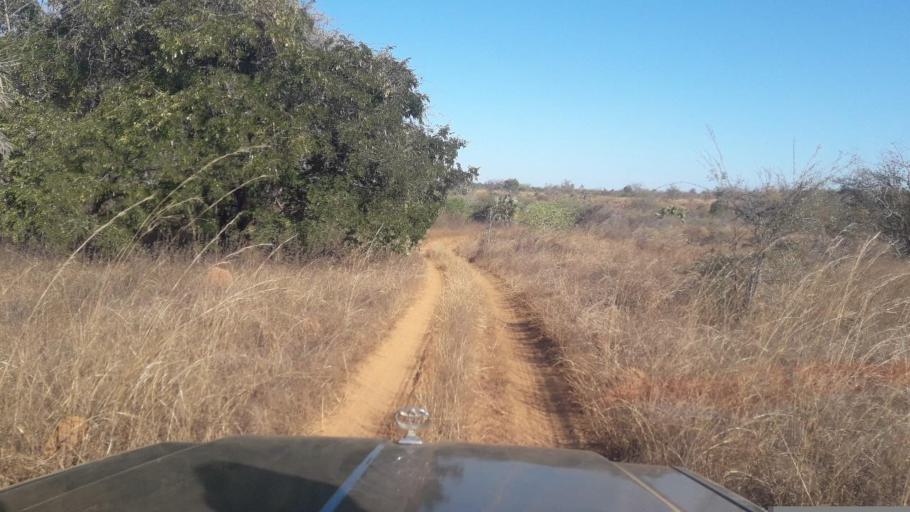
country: MG
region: Boeny
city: Sitampiky
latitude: -16.4160
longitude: 45.6094
